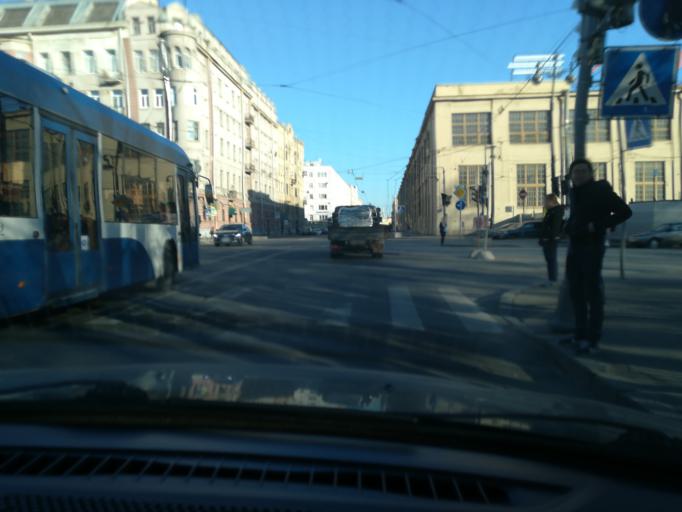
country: RU
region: St.-Petersburg
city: Vasyl'evsky Ostrov
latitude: 59.9332
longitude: 30.2622
